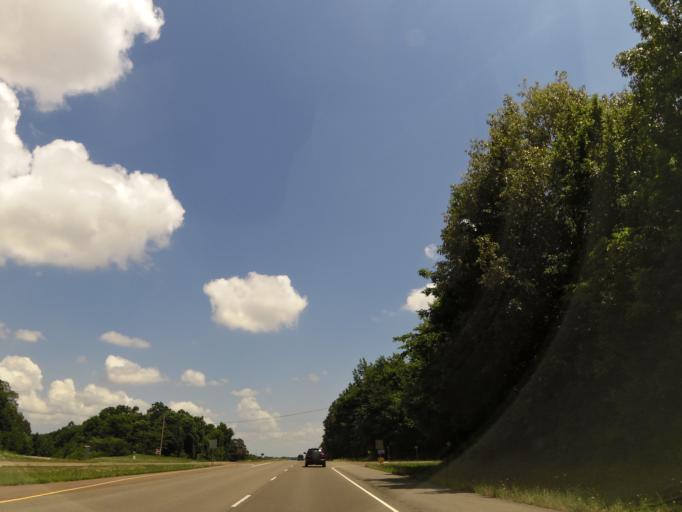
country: US
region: Tennessee
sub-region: Lauderdale County
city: Halls
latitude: 35.9098
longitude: -89.2622
